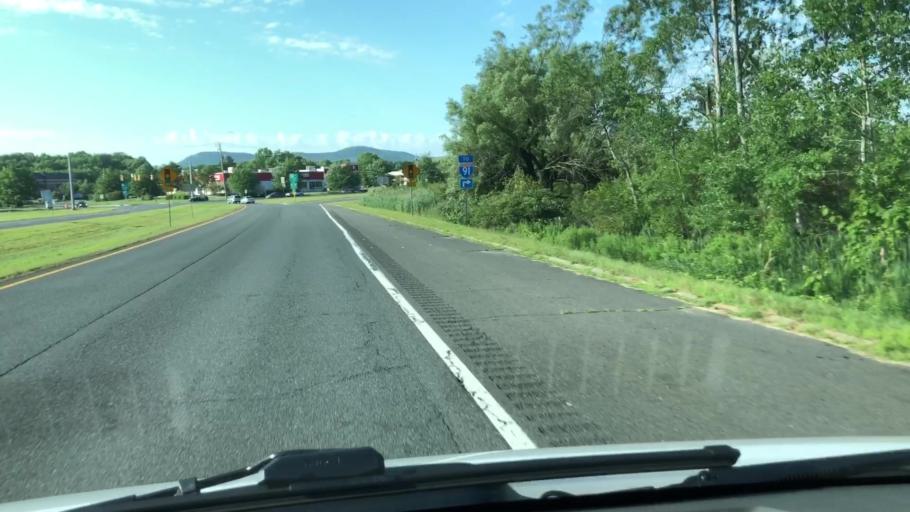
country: US
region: Massachusetts
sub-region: Hampshire County
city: Amherst Center
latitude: 42.3634
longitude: -72.5434
